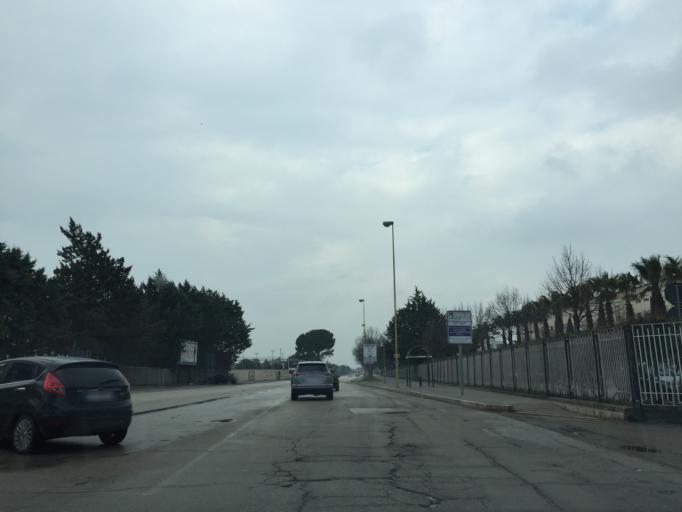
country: IT
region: Apulia
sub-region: Provincia di Foggia
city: Foggia
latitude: 41.4554
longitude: 15.5266
